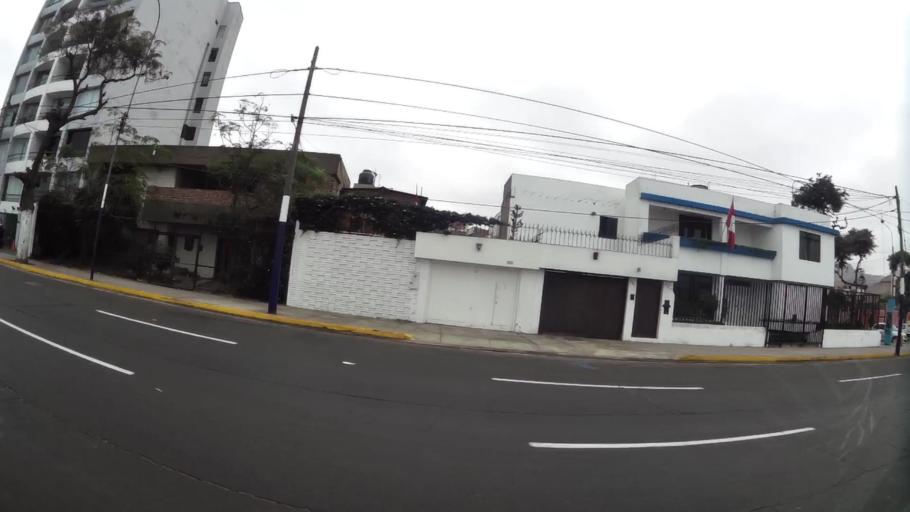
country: PE
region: Lima
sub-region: Lima
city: Surco
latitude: -12.1662
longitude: -77.0266
